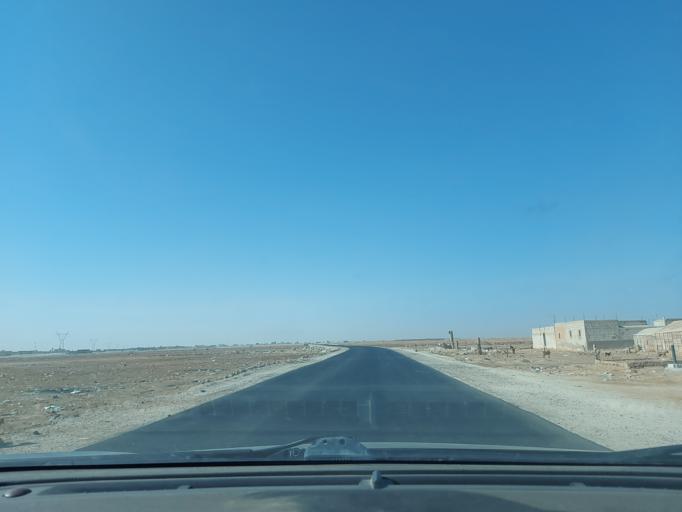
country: MR
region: Nouakchott
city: Nouakchott
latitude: 18.0077
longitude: -15.9879
